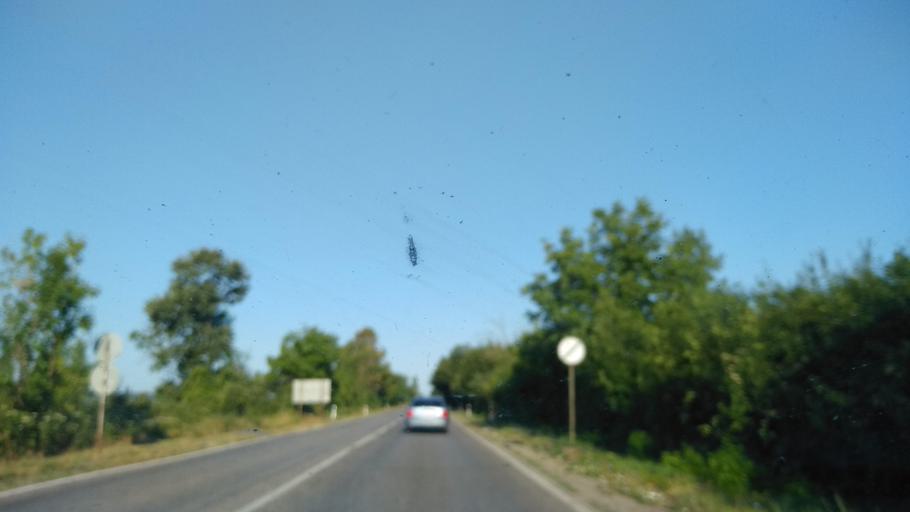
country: BG
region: Gabrovo
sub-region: Obshtina Dryanovo
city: Dryanovo
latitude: 43.0880
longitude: 25.4611
